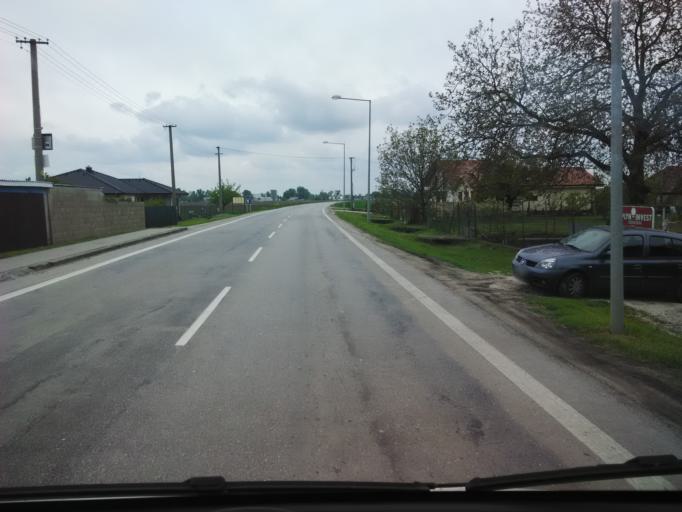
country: SK
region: Trnavsky
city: Leopoldov
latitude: 48.4731
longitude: 17.7749
